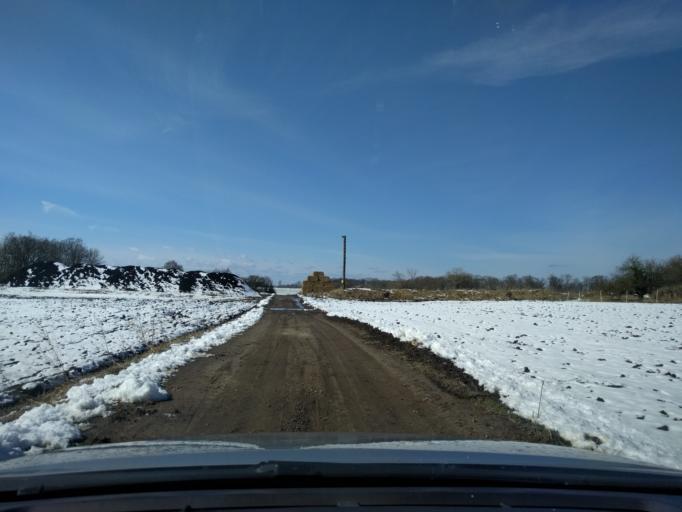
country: DK
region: South Denmark
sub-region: Nyborg Kommune
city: Ullerslev
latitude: 55.3706
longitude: 10.7207
